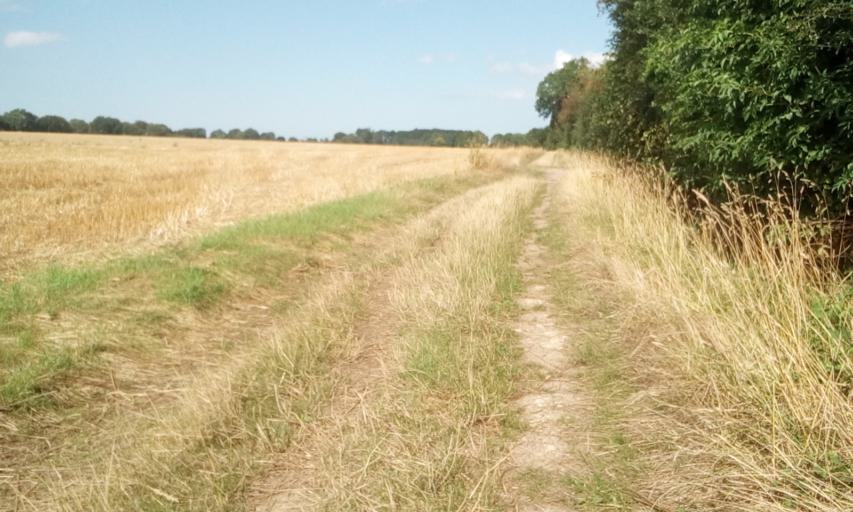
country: FR
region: Lower Normandy
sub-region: Departement du Calvados
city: Argences
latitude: 49.1348
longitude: -0.1147
